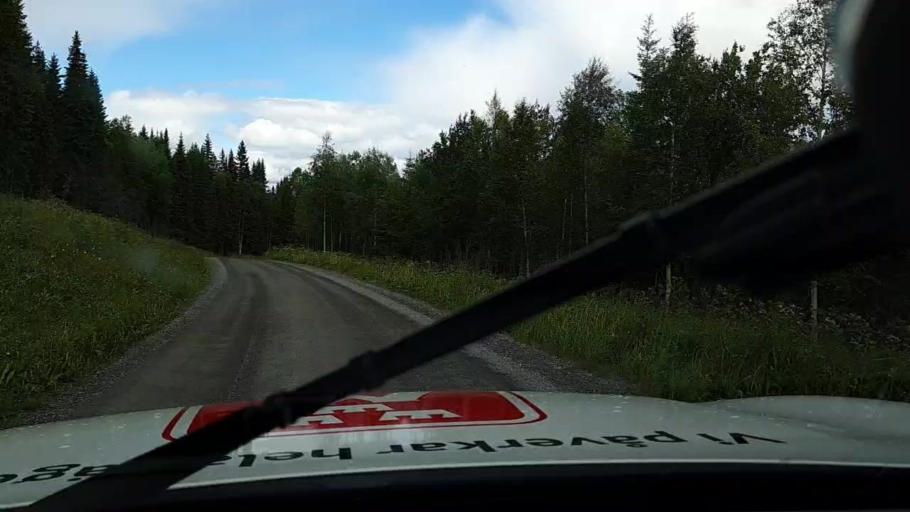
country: SE
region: Jaemtland
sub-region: Krokoms Kommun
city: Valla
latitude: 63.3931
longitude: 14.0634
